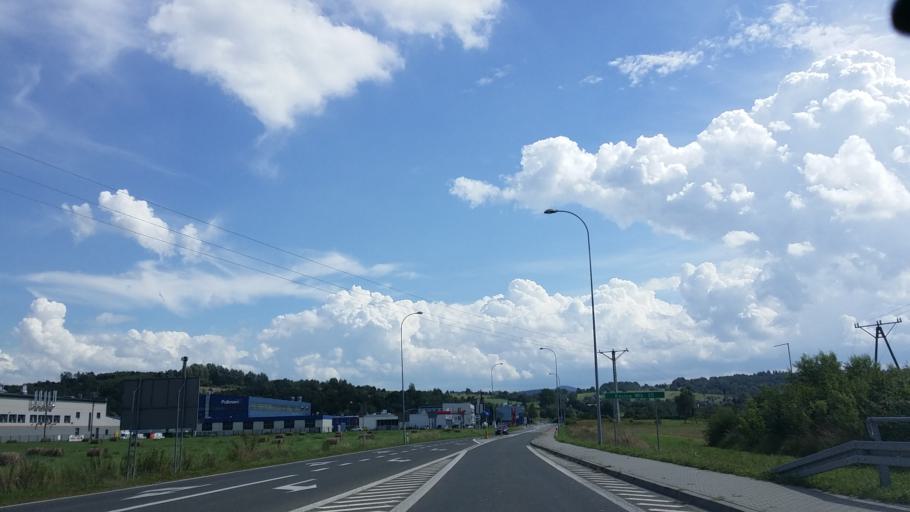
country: PL
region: Lesser Poland Voivodeship
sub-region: Powiat myslenicki
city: Dobczyce
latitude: 49.8882
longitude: 20.1012
